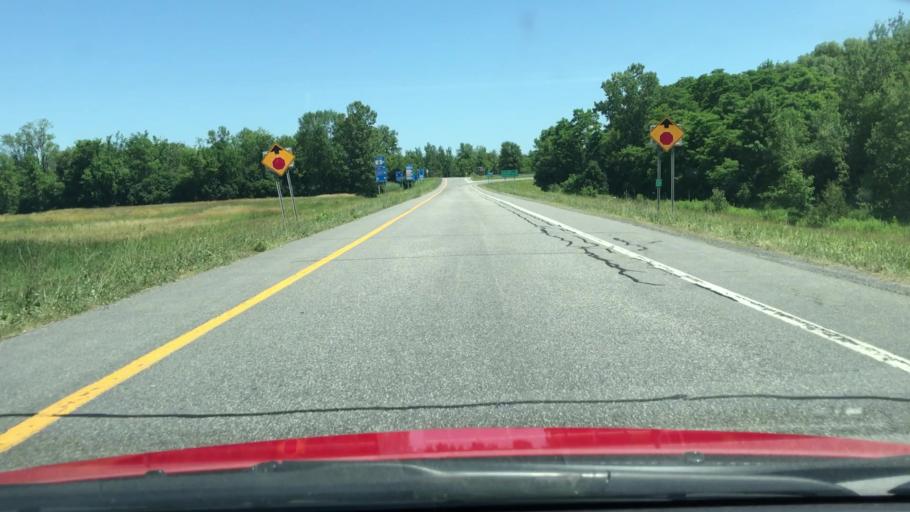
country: US
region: New York
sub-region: Clinton County
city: Plattsburgh
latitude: 44.7264
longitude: -73.4421
